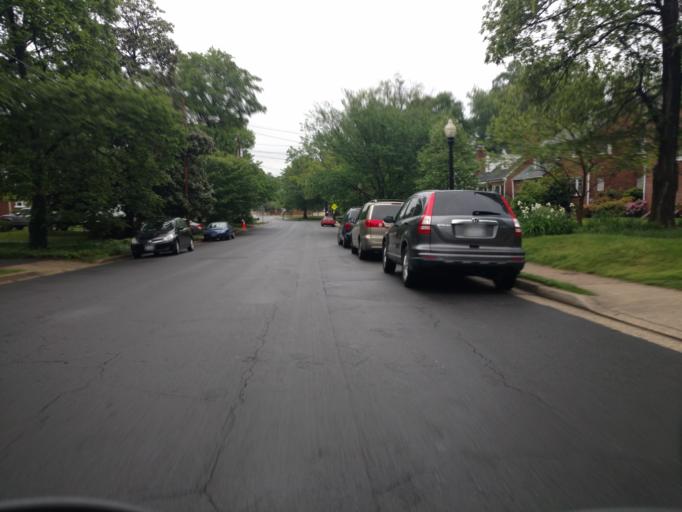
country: US
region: Virginia
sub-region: Arlington County
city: Arlington
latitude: 38.8672
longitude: -77.0830
